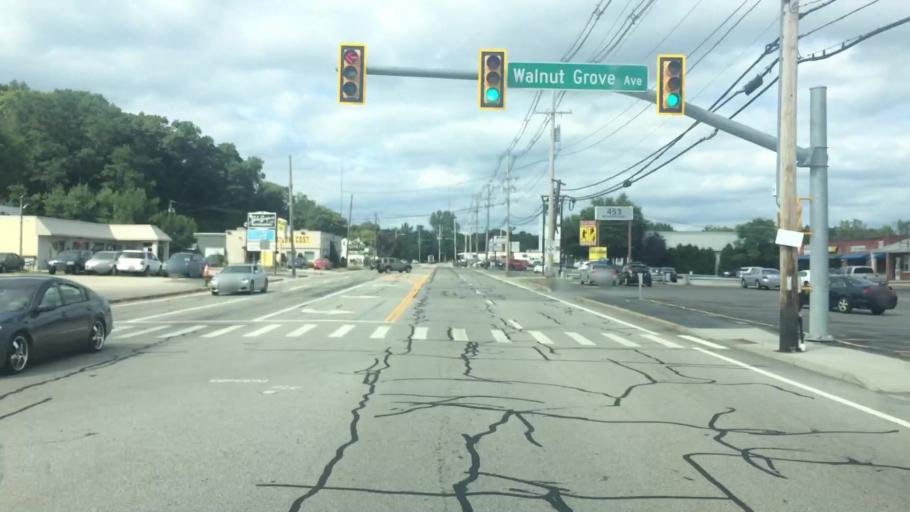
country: US
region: Rhode Island
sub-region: Providence County
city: Cranston
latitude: 41.7880
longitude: -71.4723
